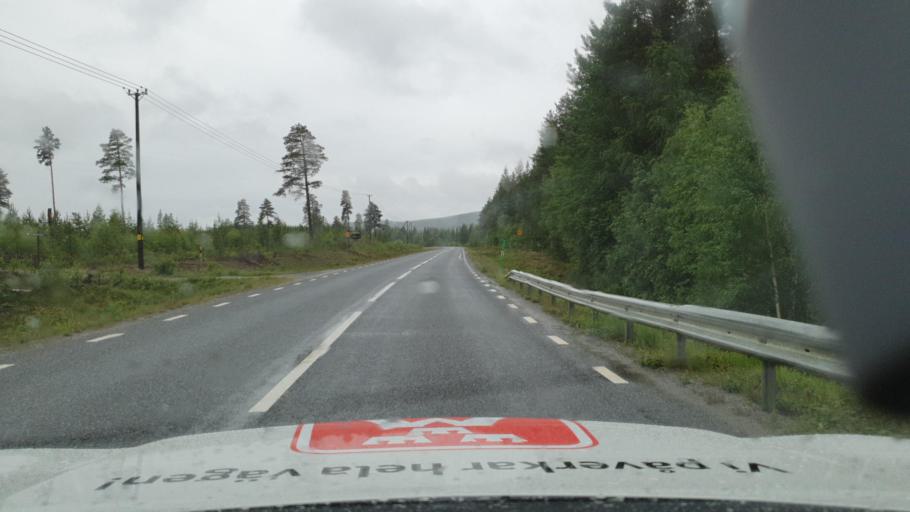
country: SE
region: Vaesterbotten
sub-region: Asele Kommun
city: Asele
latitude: 64.0029
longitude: 17.2731
